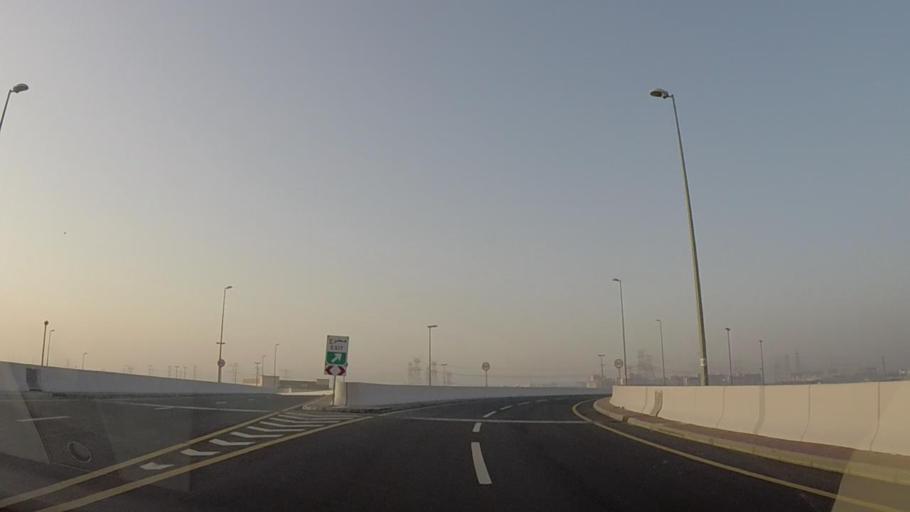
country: AE
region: Dubai
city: Dubai
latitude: 25.0580
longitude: 55.1390
